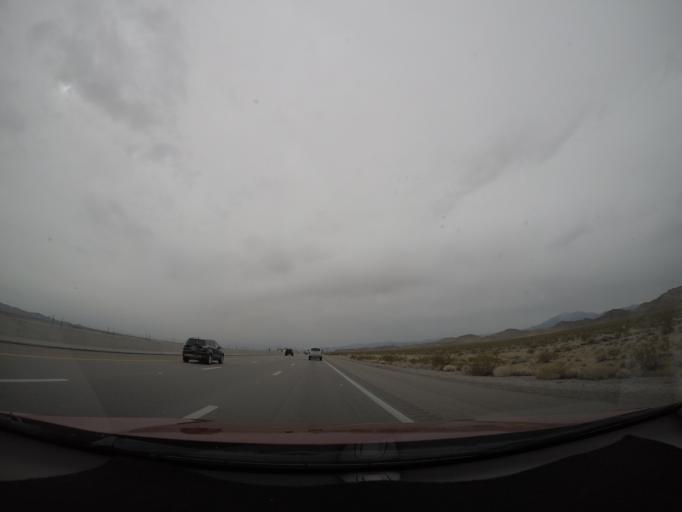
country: US
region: Nevada
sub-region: Clark County
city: Sandy Valley
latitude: 35.6433
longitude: -115.3833
